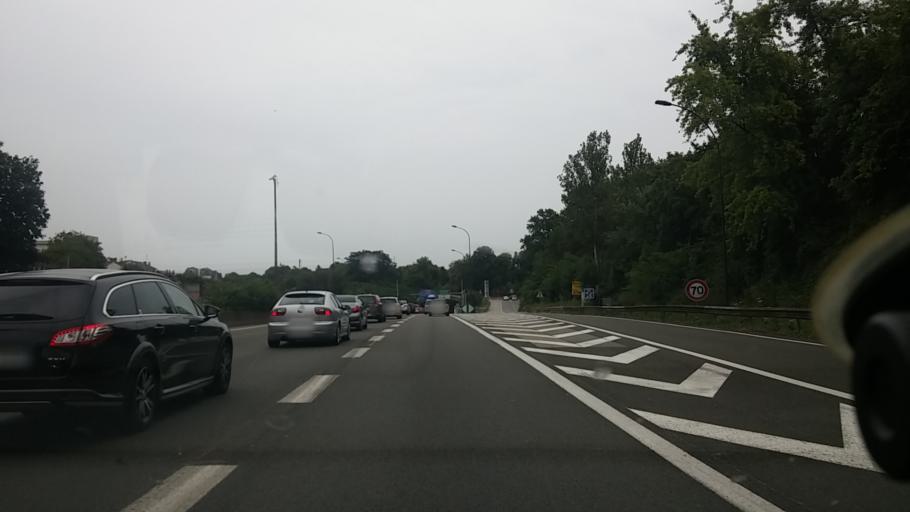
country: FR
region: Ile-de-France
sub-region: Departement des Hauts-de-Seine
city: Saint-Cloud
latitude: 48.8396
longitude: 2.2017
